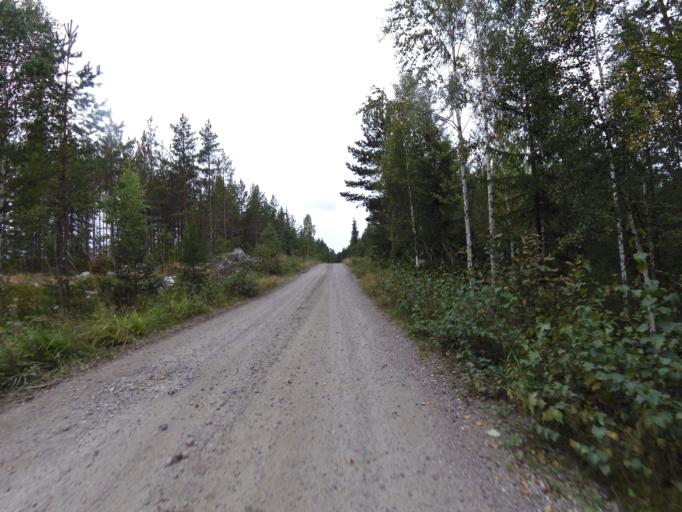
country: SE
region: Gaevleborg
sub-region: Gavle Kommun
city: Valbo
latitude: 60.7315
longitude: 17.0600
